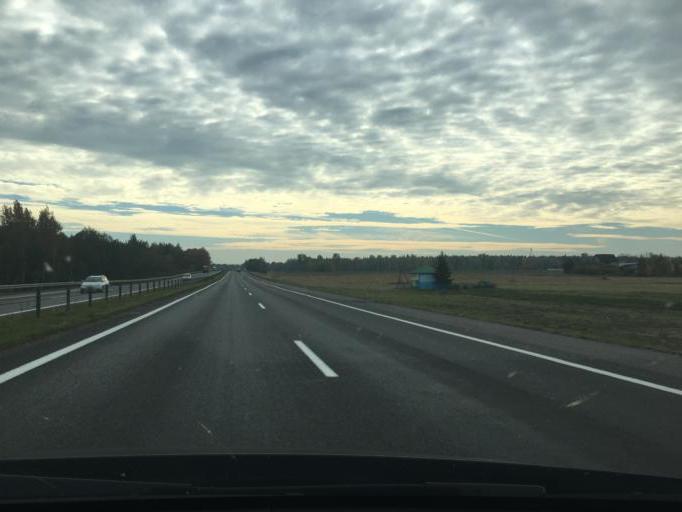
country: BY
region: Minsk
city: Enyerhyetykaw
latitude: 53.6040
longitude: 27.0457
